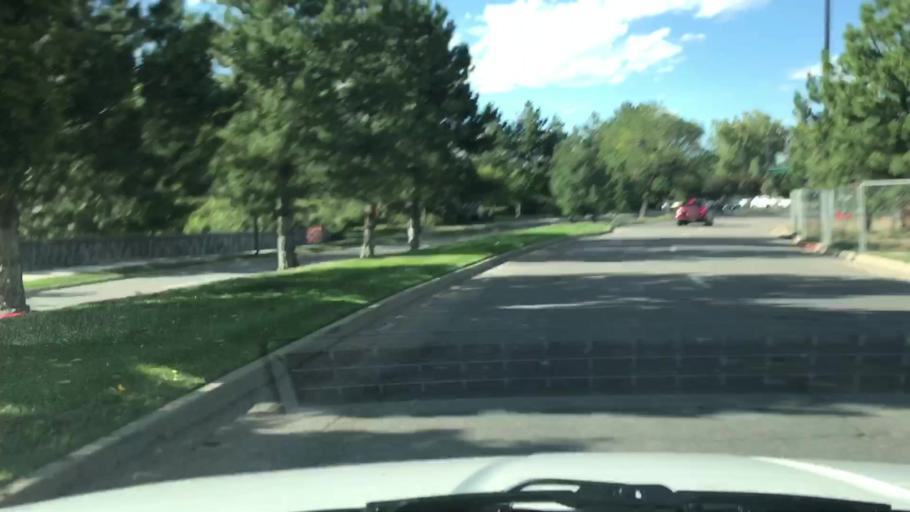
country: US
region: Colorado
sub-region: Arapahoe County
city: Greenwood Village
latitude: 39.6368
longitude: -104.9129
